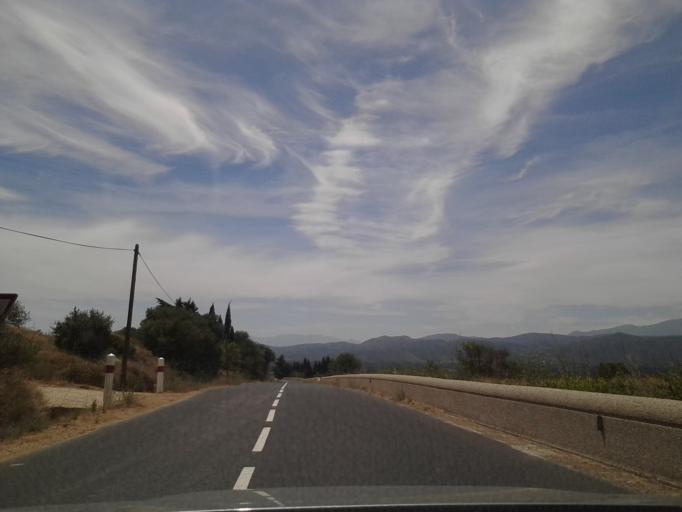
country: FR
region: Languedoc-Roussillon
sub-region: Departement des Pyrenees-Orientales
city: Millas
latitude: 42.7104
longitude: 2.6836
